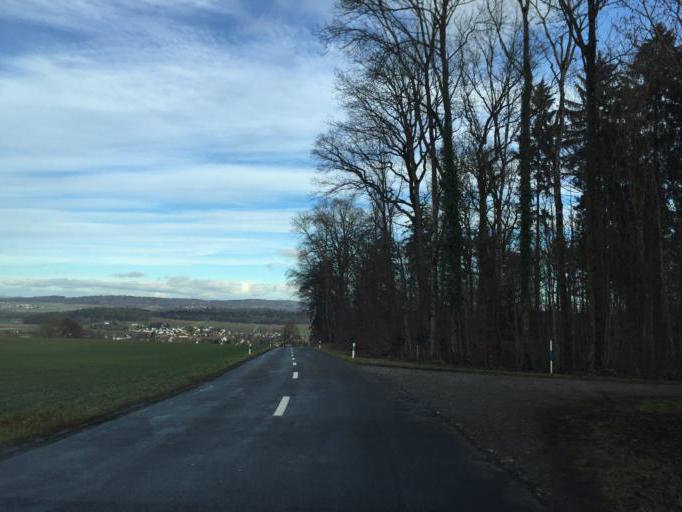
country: CH
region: Zurich
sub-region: Bezirk Andelfingen
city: Marthalen
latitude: 47.6514
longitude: 8.6886
